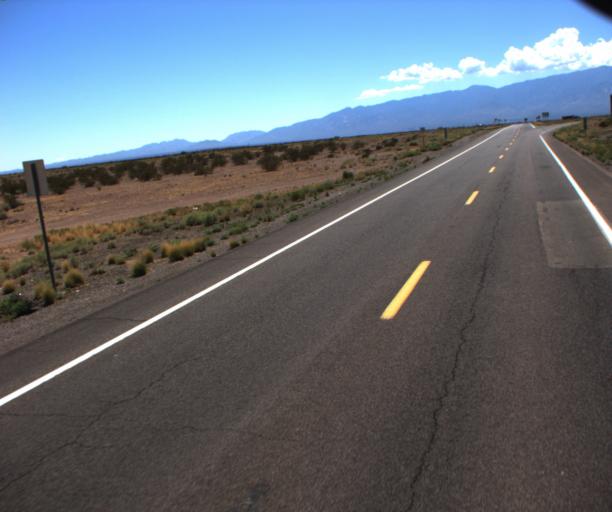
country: US
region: Arizona
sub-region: Graham County
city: Safford
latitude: 32.7933
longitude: -109.5464
